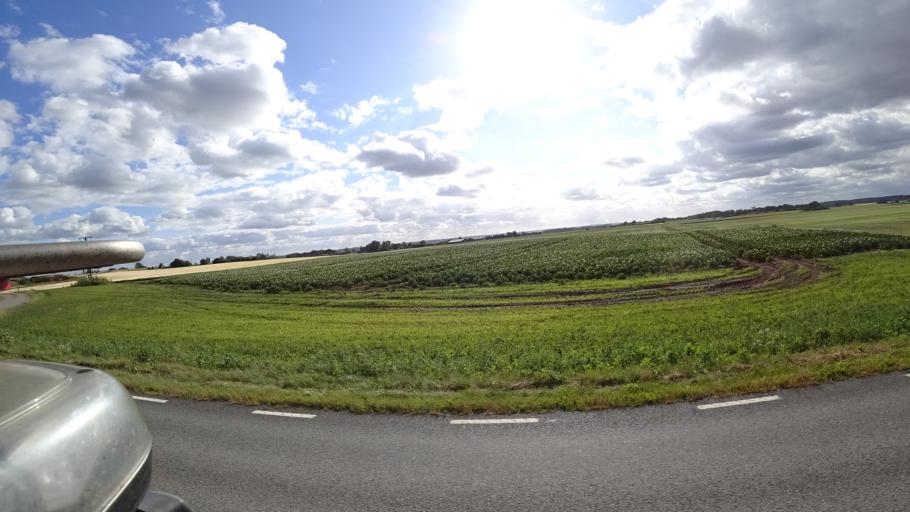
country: SE
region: Skane
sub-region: Kristianstads Kommun
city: Onnestad
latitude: 56.0860
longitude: 14.0806
